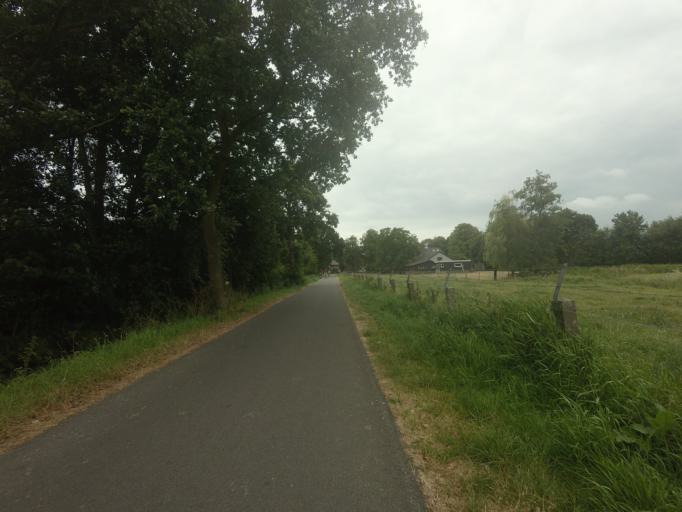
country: NL
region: Utrecht
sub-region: Gemeente De Bilt
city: De Bilt
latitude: 52.1595
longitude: 5.1757
